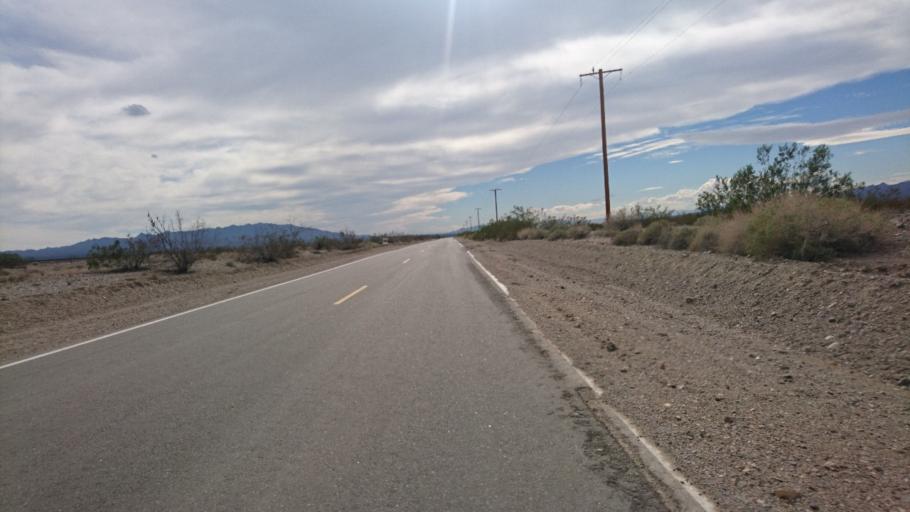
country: US
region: California
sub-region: San Bernardino County
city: Needles
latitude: 34.7873
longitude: -115.2033
